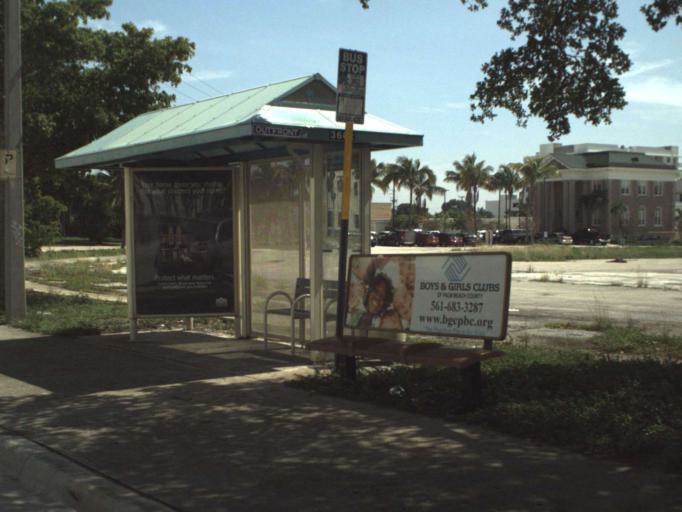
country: US
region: Florida
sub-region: Palm Beach County
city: West Palm Beach
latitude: 26.7173
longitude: -80.0550
